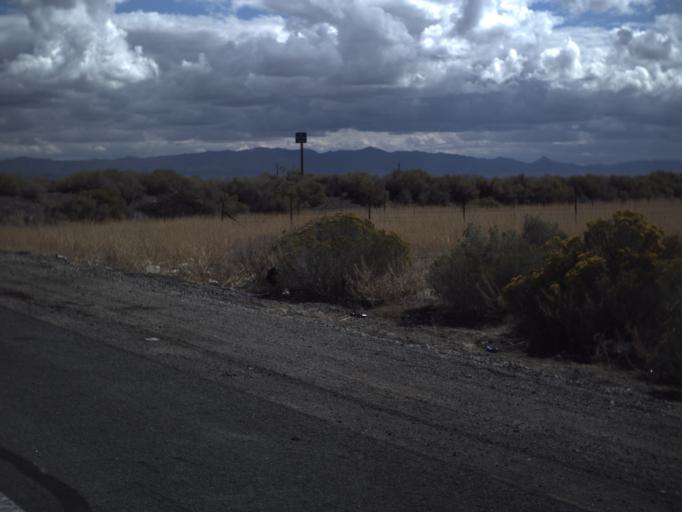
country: US
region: Utah
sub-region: Tooele County
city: Wendover
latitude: 40.7259
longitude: -113.2595
